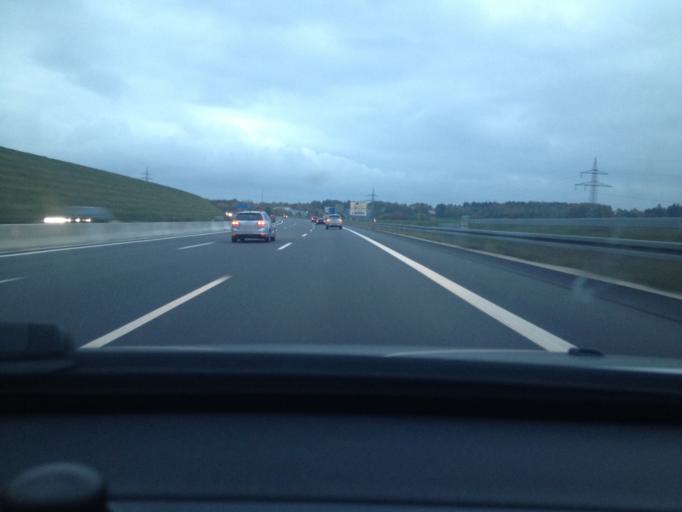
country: DE
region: Baden-Wuerttemberg
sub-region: Tuebingen Region
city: Dornstadt
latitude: 48.4575
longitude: 9.9444
